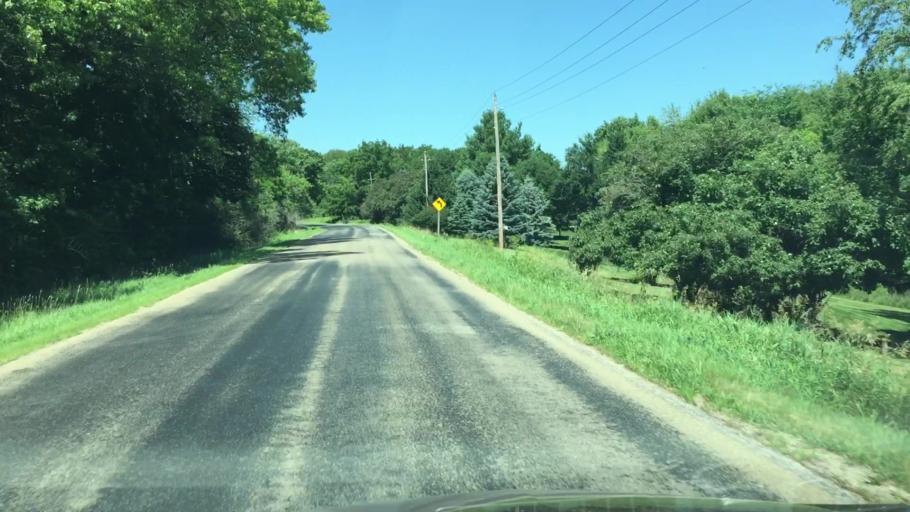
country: US
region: Iowa
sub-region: Linn County
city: Ely
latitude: 41.8160
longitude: -91.6060
